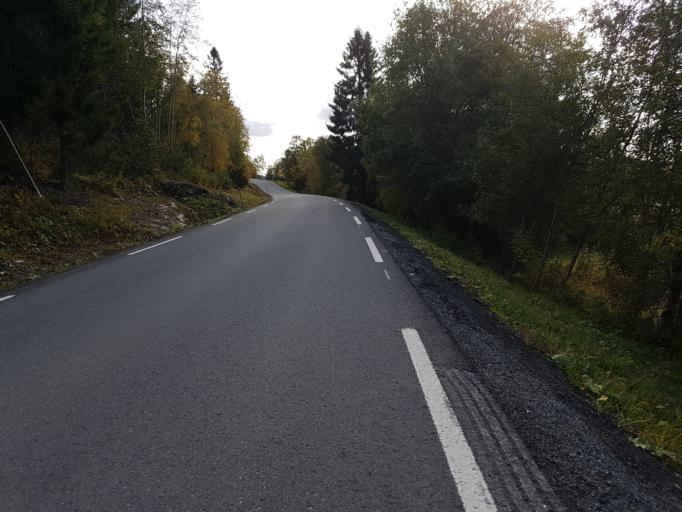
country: NO
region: Sor-Trondelag
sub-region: Malvik
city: Malvik
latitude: 63.3655
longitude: 10.6233
